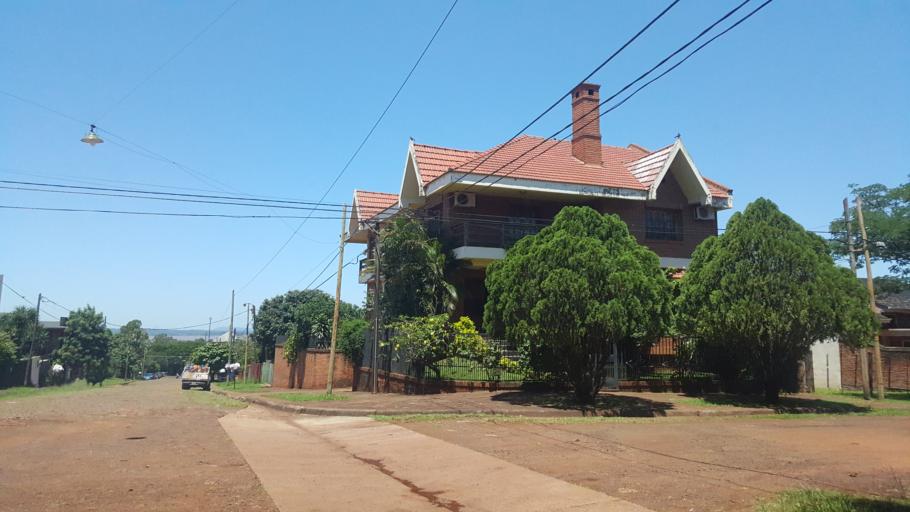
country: AR
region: Misiones
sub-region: Departamento de Capital
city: Posadas
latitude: -27.3940
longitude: -55.9118
